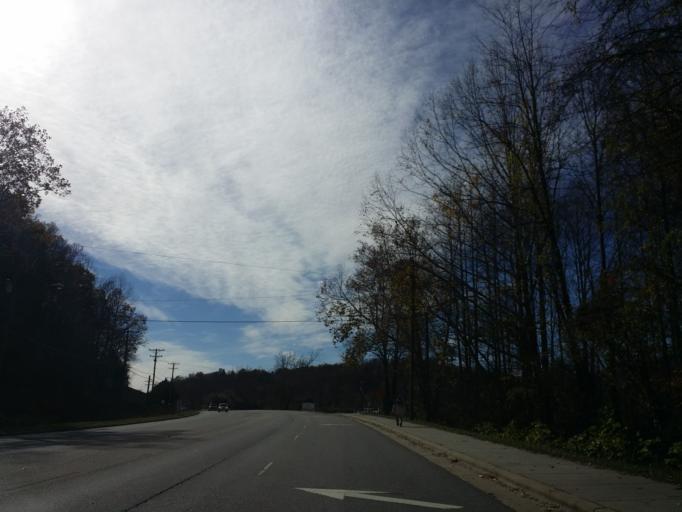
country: US
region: North Carolina
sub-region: McDowell County
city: Marion
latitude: 35.7002
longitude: -82.0448
